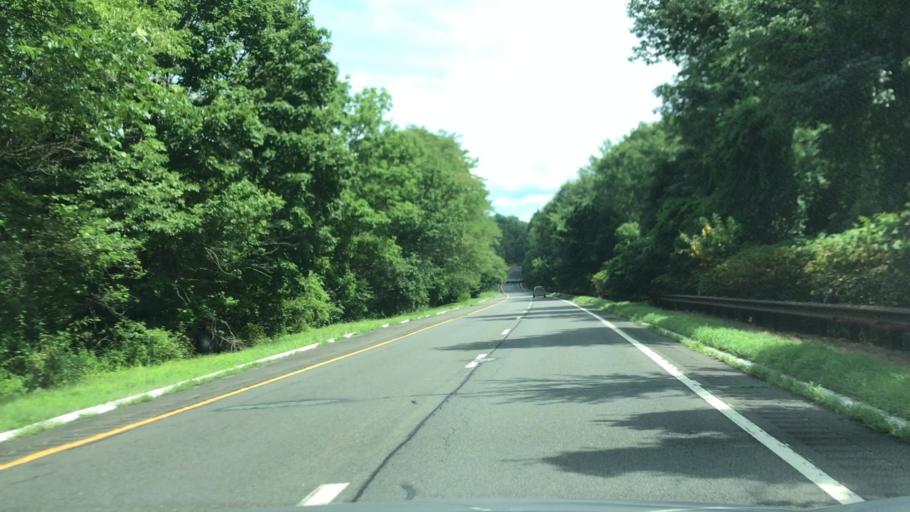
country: US
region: New York
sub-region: Rockland County
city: Sparkill
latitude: 41.0201
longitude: -73.9323
